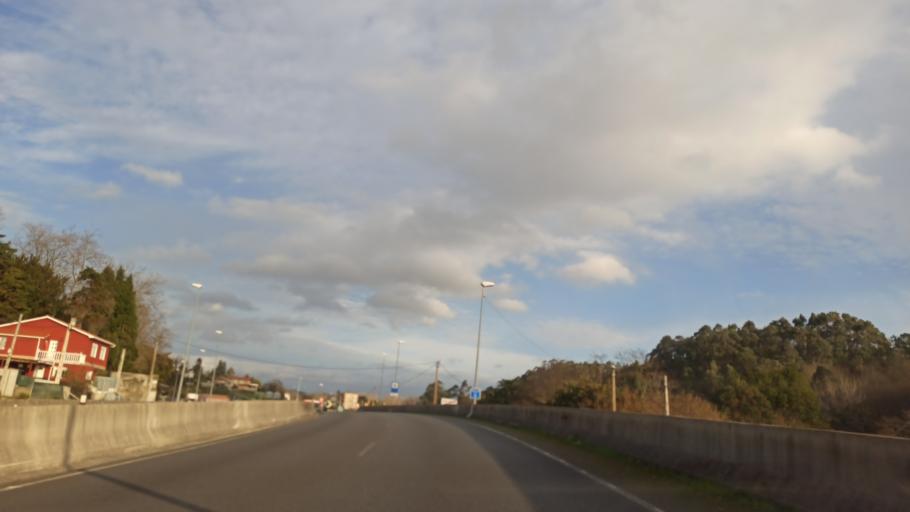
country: ES
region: Galicia
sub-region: Provincia da Coruna
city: Cambre
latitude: 43.3223
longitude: -8.3455
